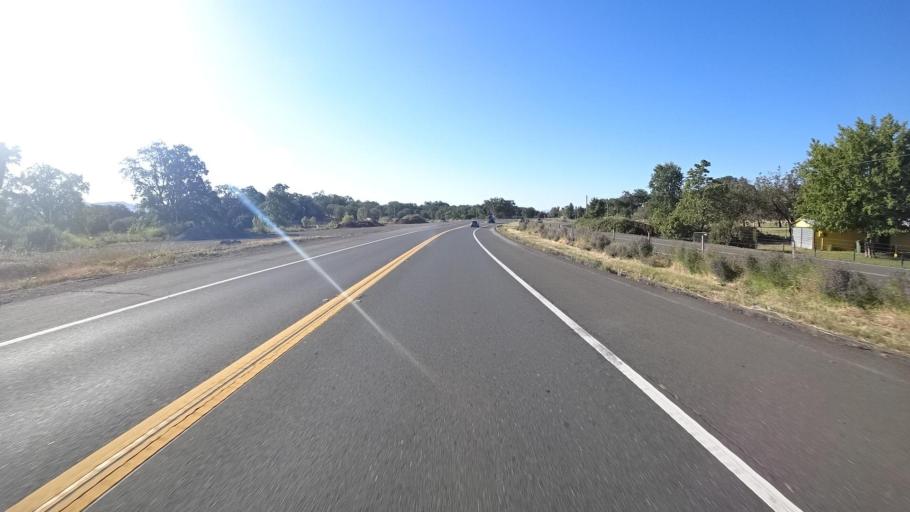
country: US
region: California
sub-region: Lake County
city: Upper Lake
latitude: 39.1392
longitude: -122.9112
